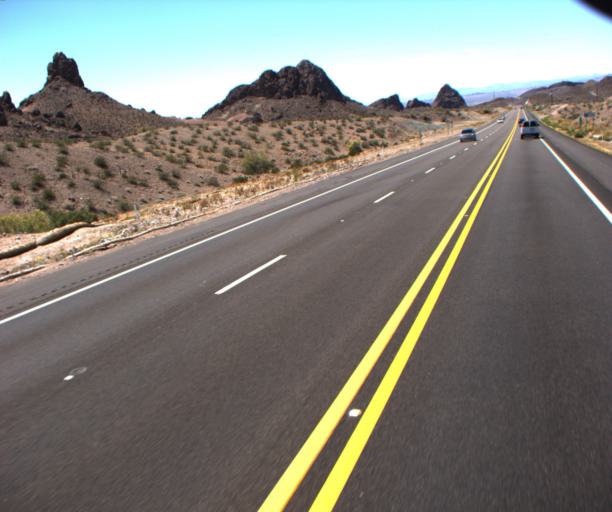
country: US
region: Arizona
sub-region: Mohave County
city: Desert Hills
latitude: 34.6234
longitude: -114.3362
